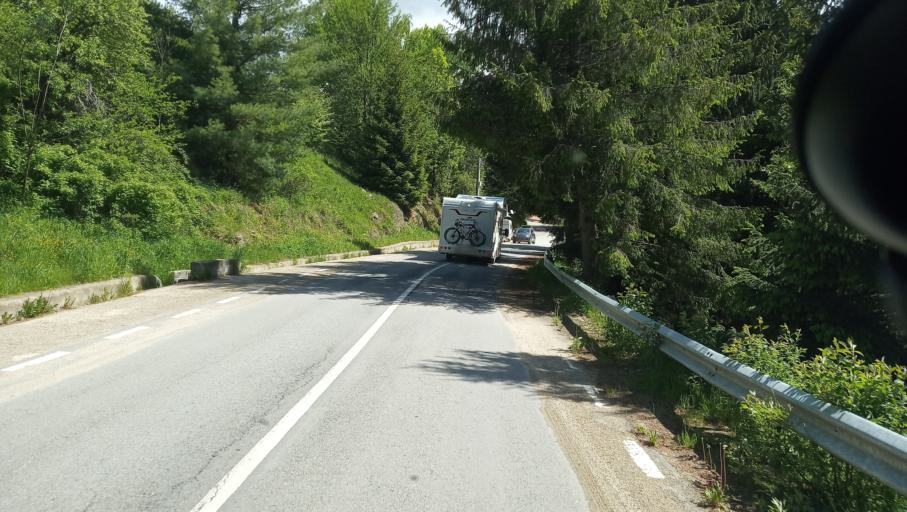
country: RO
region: Caras-Severin
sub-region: Comuna Brebu Nou
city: Brebu Nou
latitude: 45.2184
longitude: 22.1053
